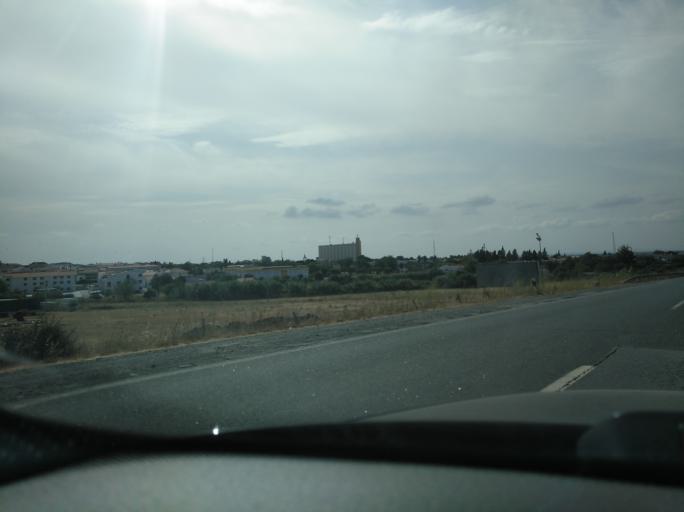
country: PT
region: Beja
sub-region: Beja
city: Ferreira do Alentejo
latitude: 38.0641
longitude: -8.1104
